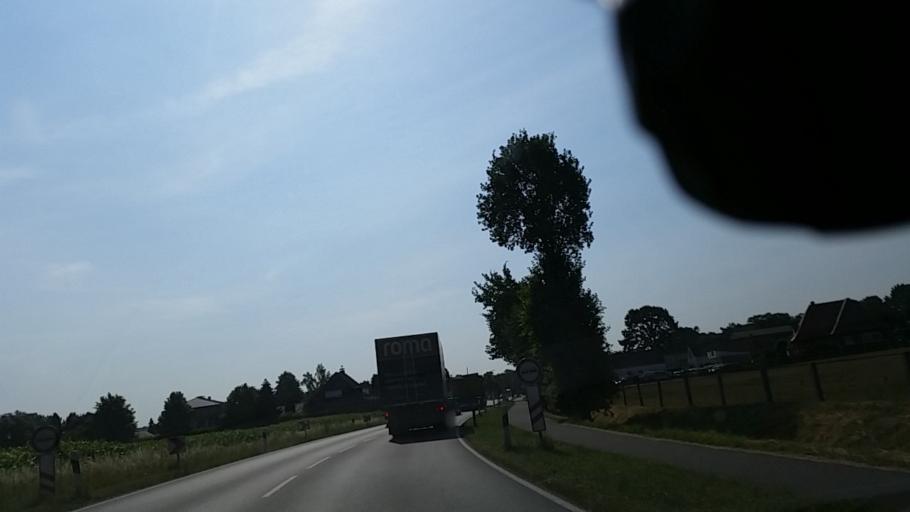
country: DE
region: Lower Saxony
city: Steinfeld
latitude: 52.5931
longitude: 8.1953
